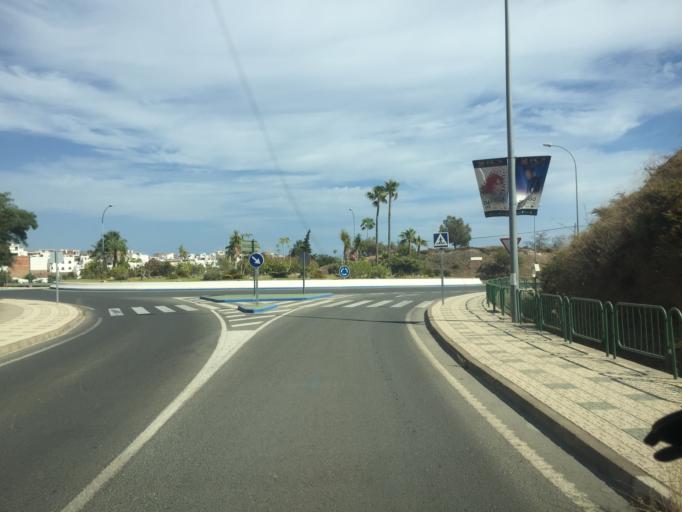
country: ES
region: Andalusia
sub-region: Provincia de Malaga
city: Nerja
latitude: 36.7596
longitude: -3.8472
